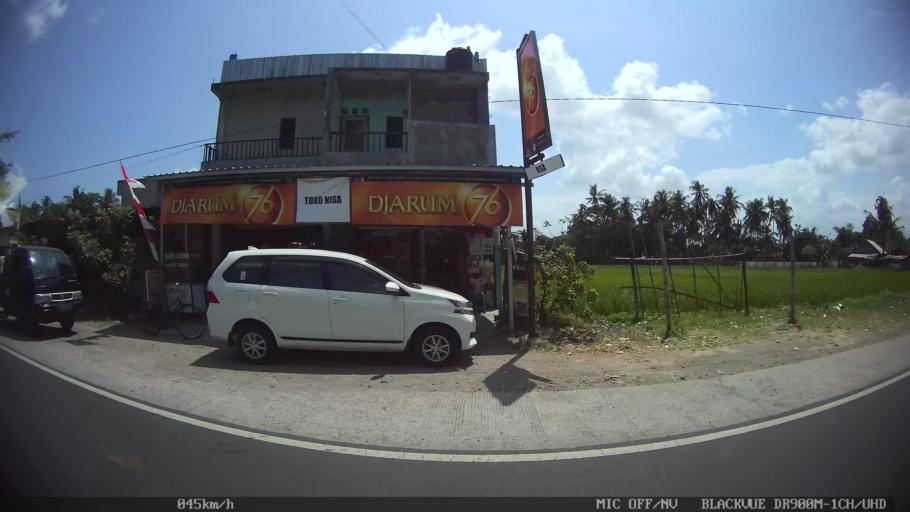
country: ID
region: Daerah Istimewa Yogyakarta
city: Pundong
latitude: -7.9225
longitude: 110.3750
